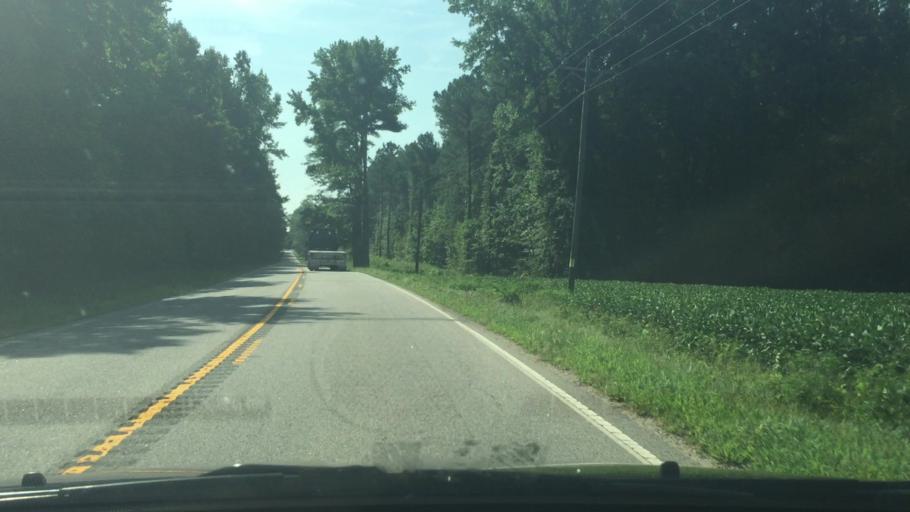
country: US
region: Virginia
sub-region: Sussex County
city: Sussex
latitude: 37.0053
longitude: -77.2692
